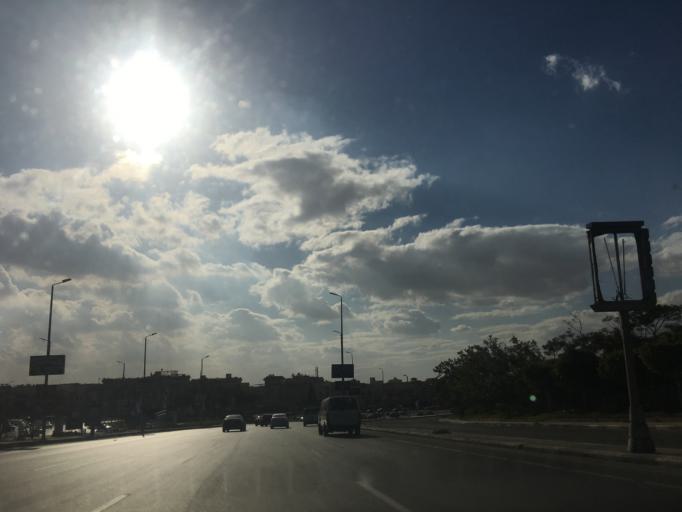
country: EG
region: Muhafazat al Qahirah
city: Cairo
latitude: 30.0175
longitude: 31.4468
